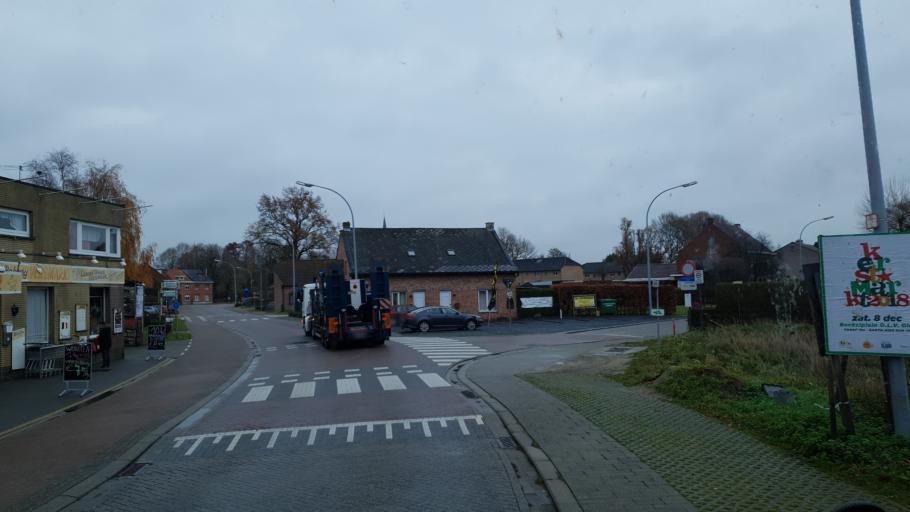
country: BE
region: Flanders
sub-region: Provincie Antwerpen
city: Olen
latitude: 51.1660
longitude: 4.8964
